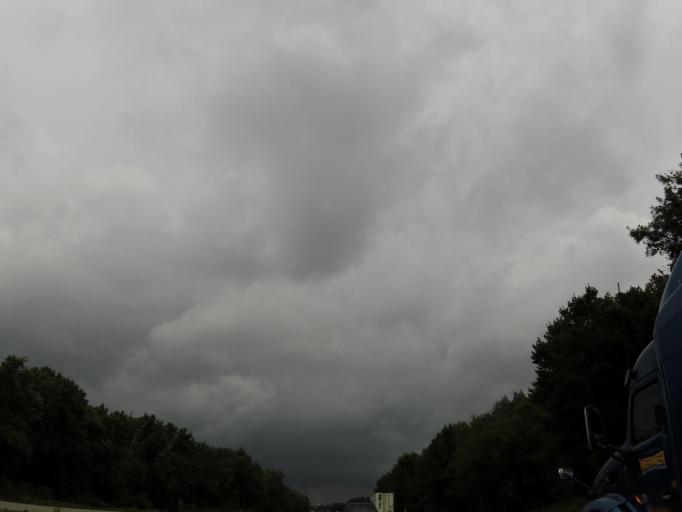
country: US
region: Illinois
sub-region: Jefferson County
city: Ina
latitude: 38.2142
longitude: -88.9090
